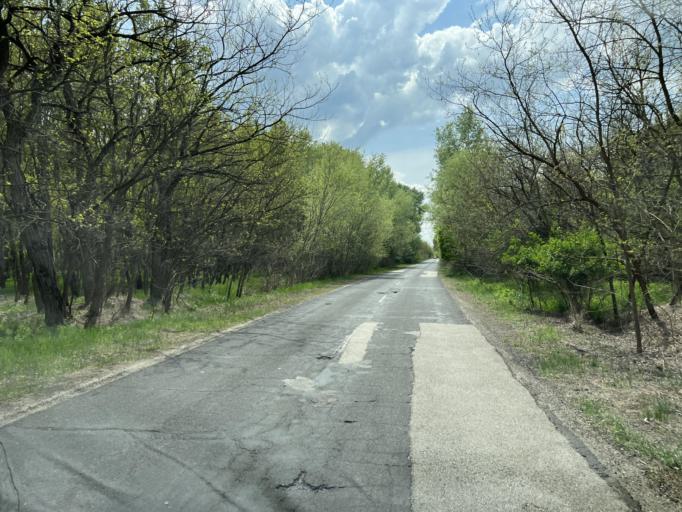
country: HU
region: Pest
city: Csemo
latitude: 47.1185
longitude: 19.6517
